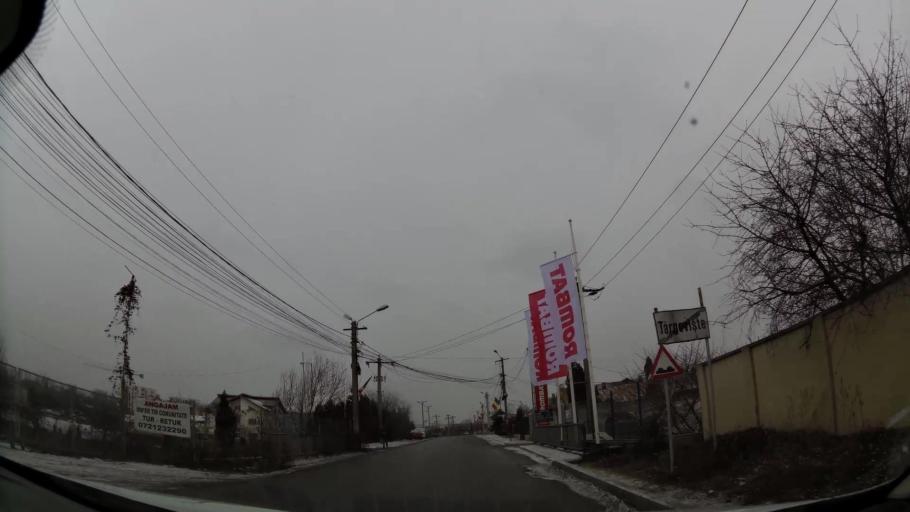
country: RO
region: Dambovita
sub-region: Municipiul Targoviste
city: Targoviste
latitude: 44.9392
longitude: 25.4655
